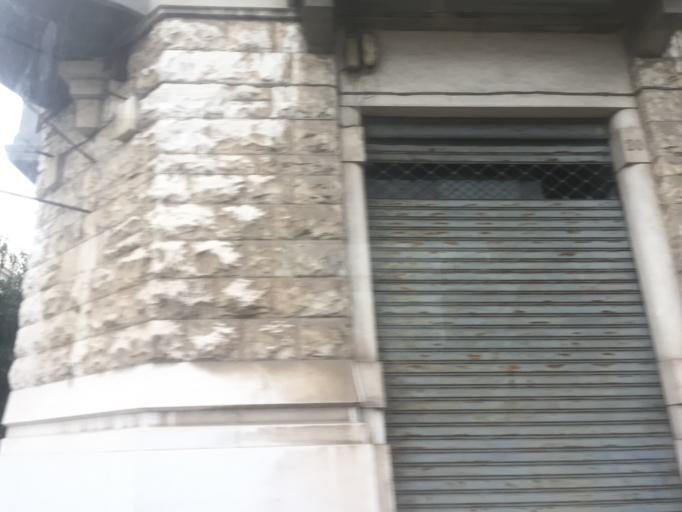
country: IT
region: Apulia
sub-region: Provincia di Bari
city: Bari
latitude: 41.1277
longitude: 16.8654
